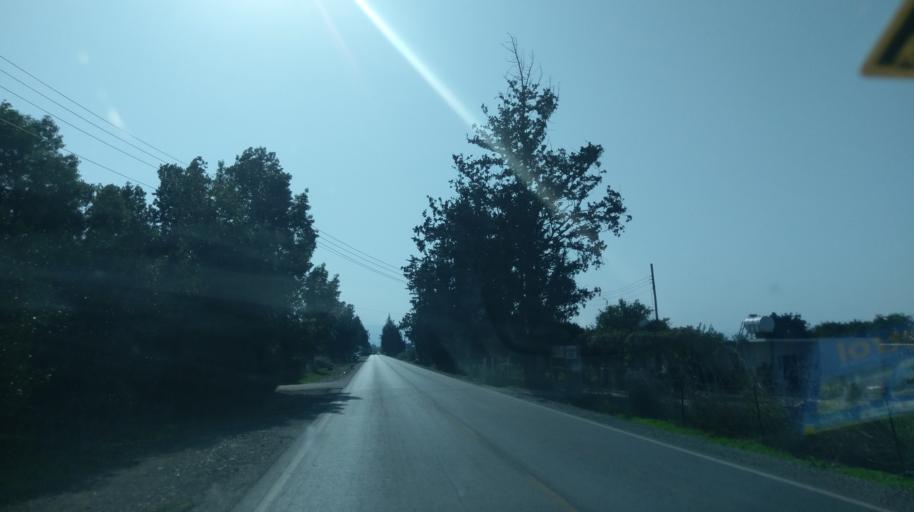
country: CY
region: Lefkosia
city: Morfou
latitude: 35.2238
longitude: 33.0101
